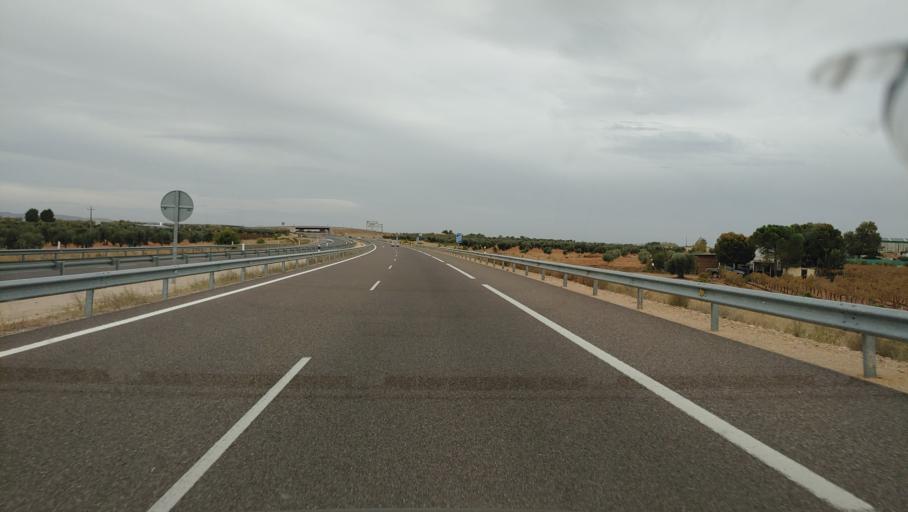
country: ES
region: Castille-La Mancha
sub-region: Provincia de Ciudad Real
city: Valenzuela de Calatrava
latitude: 38.9024
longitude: -3.8059
